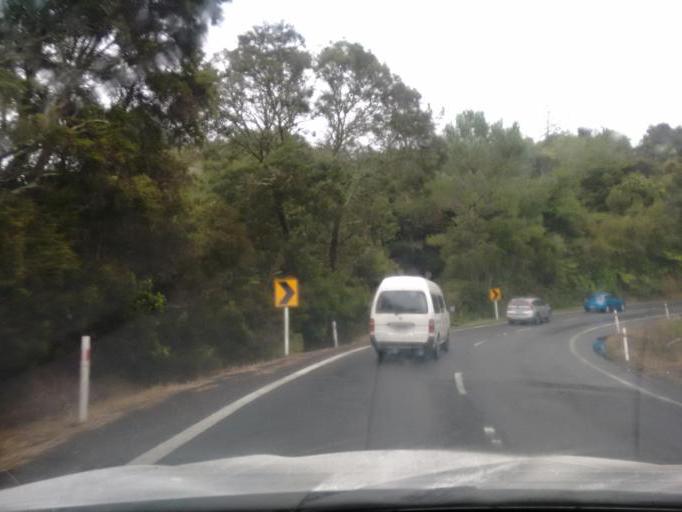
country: NZ
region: Waikato
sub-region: Thames-Coromandel District
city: Whitianga
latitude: -36.9187
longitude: 175.6826
